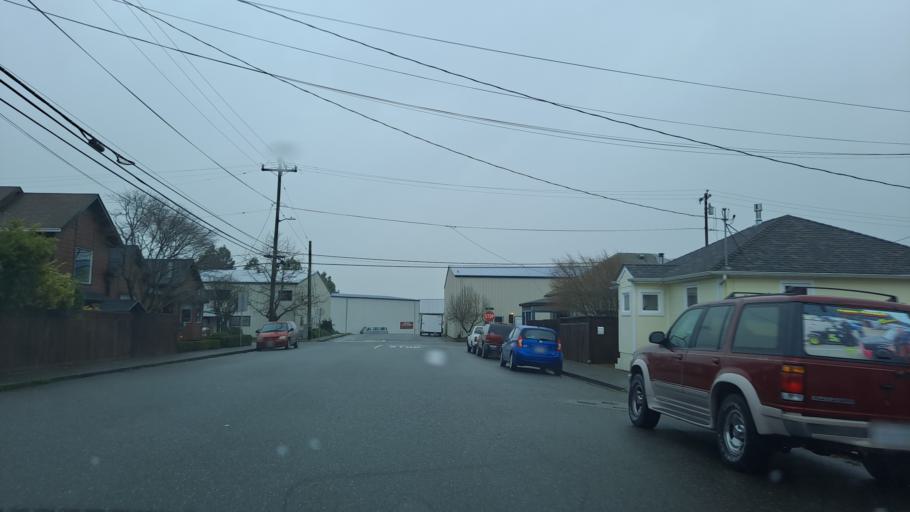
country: US
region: California
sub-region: Humboldt County
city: Fortuna
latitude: 40.5972
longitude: -124.1596
